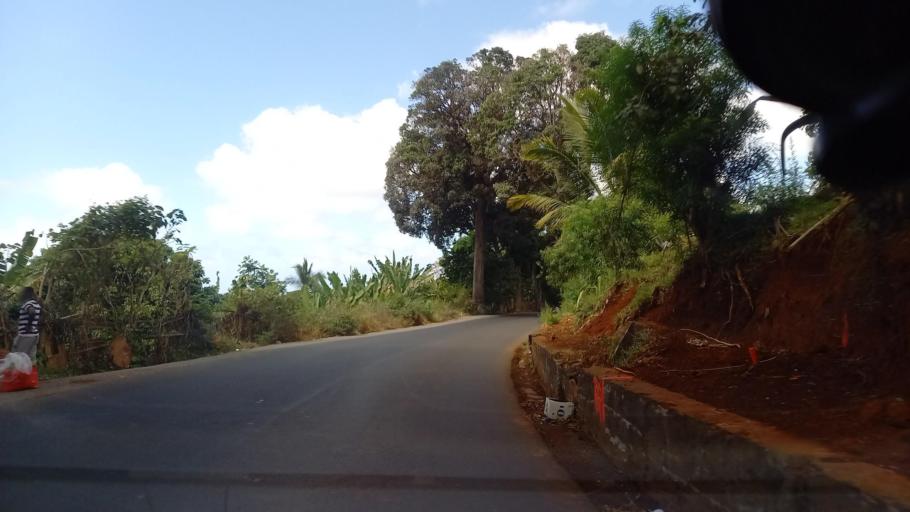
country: YT
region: Mamoudzou
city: Mamoudzou
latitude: -12.7885
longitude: 45.1777
